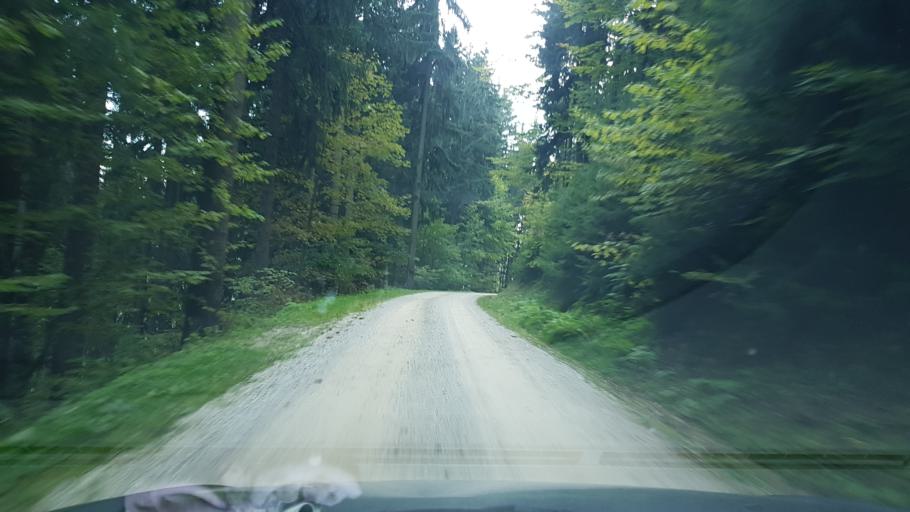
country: SI
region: Slovenj Gradec
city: Legen
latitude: 46.5257
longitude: 15.1337
